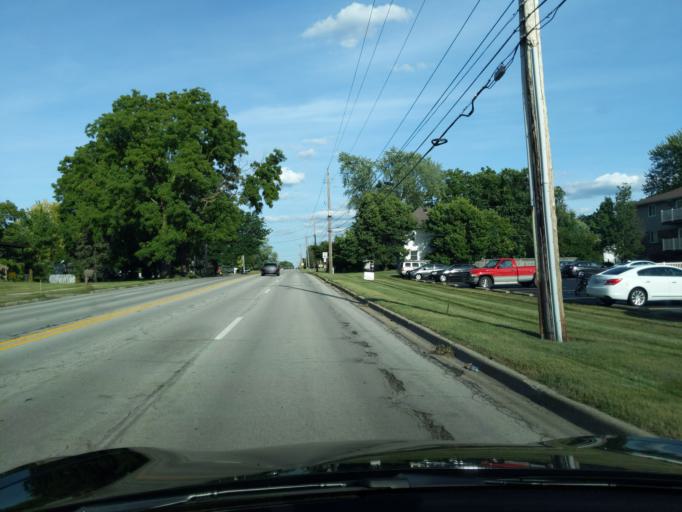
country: US
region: Michigan
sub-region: Eaton County
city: Waverly
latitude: 42.7265
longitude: -84.6313
